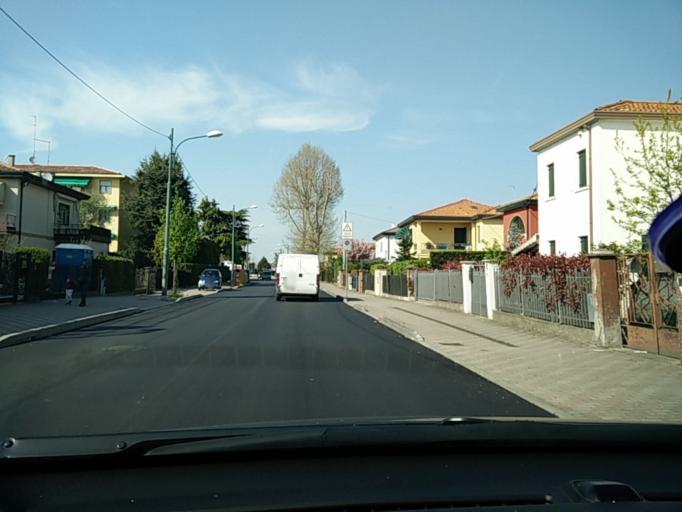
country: IT
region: Veneto
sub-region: Provincia di Venezia
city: Dese
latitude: 45.5128
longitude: 12.2833
